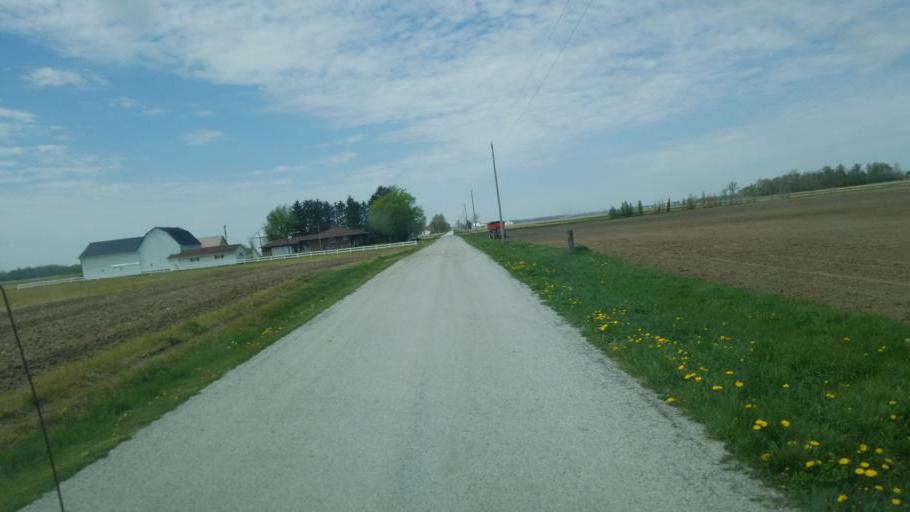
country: US
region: Ohio
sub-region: Hardin County
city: Kenton
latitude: 40.6582
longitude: -83.7399
